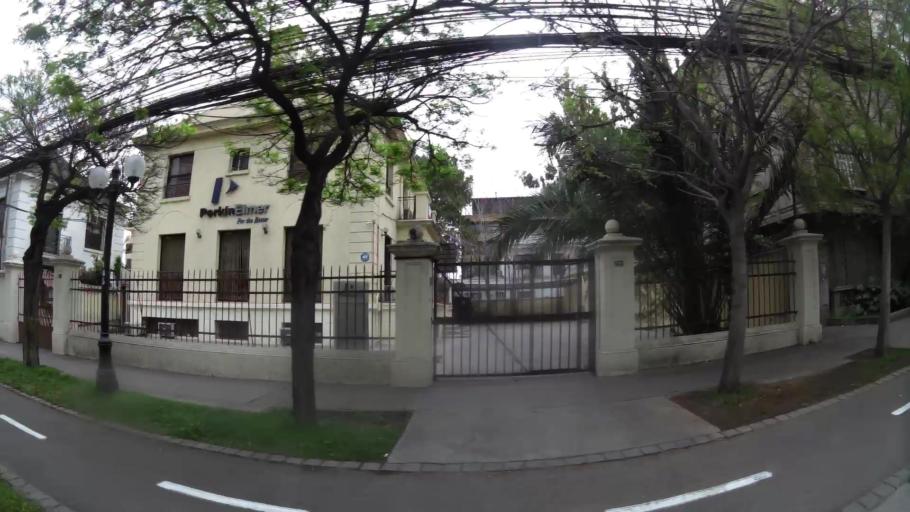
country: CL
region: Santiago Metropolitan
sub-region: Provincia de Santiago
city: Santiago
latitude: -33.4336
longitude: -70.6157
